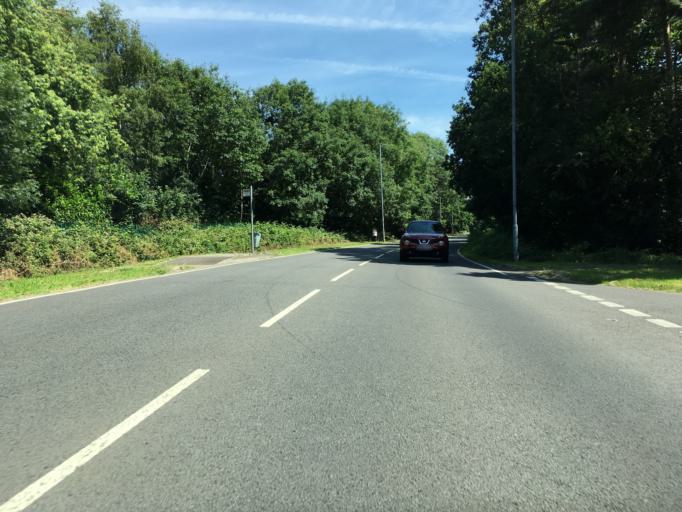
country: GB
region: Wales
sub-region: Newport
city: Newport
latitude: 51.5638
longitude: -3.0233
